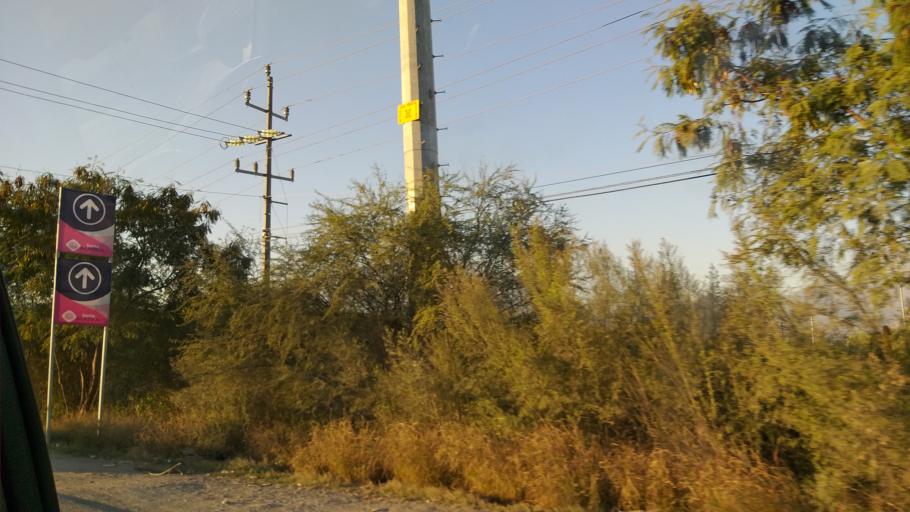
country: MX
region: Nuevo Leon
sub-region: Garcia
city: Parque Industrial Ciudad Mitras
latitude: 25.7787
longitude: -100.4478
